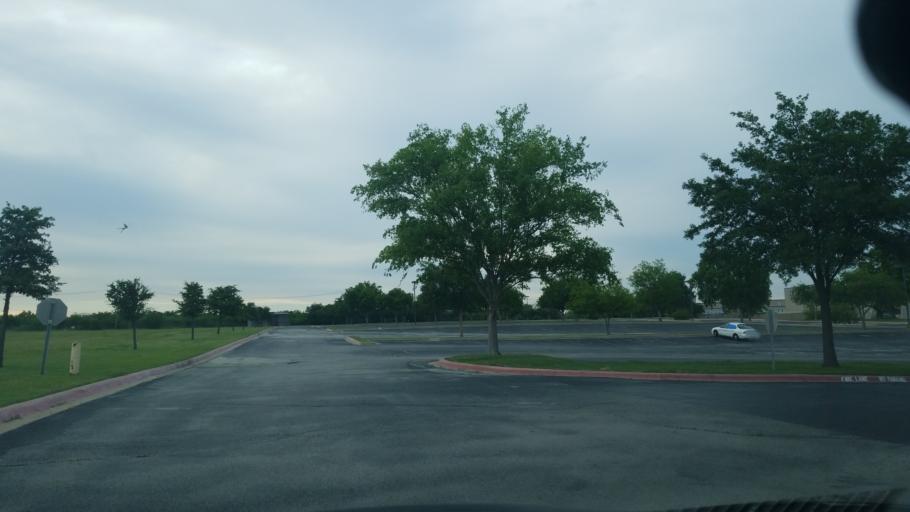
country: US
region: Texas
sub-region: Dallas County
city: Irving
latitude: 32.8717
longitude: -96.9779
